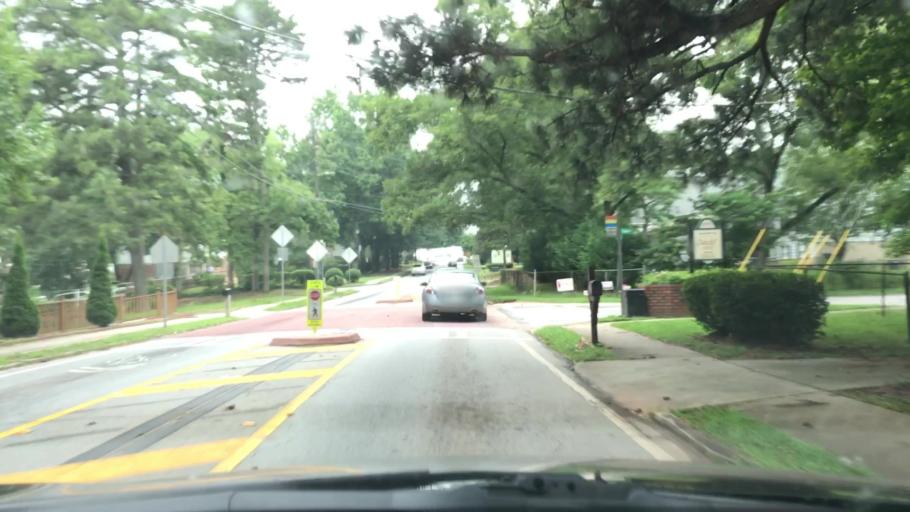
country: US
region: Georgia
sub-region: DeKalb County
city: Doraville
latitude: 33.9104
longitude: -84.2598
